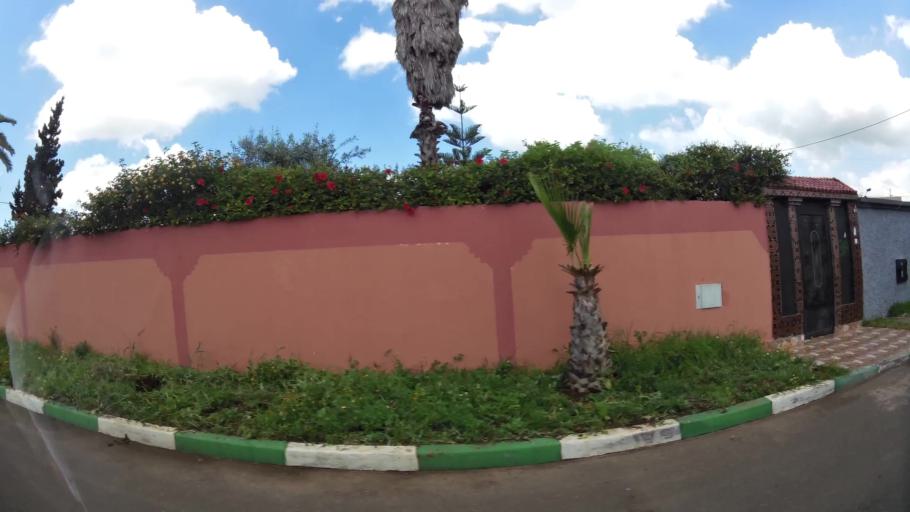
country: MA
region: Grand Casablanca
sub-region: Mediouna
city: Mediouna
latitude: 33.3828
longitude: -7.5408
